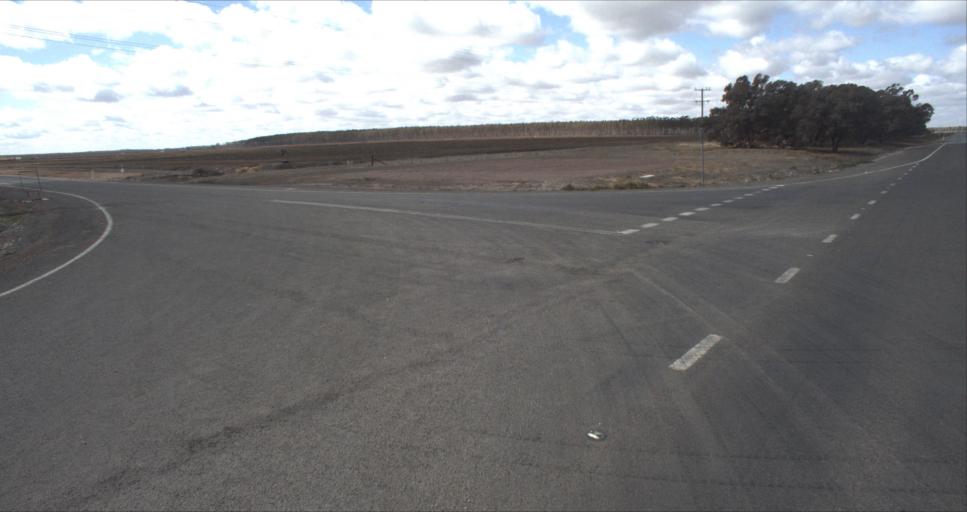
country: AU
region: New South Wales
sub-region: Murrumbidgee Shire
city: Darlington Point
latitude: -34.5744
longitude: 146.1665
